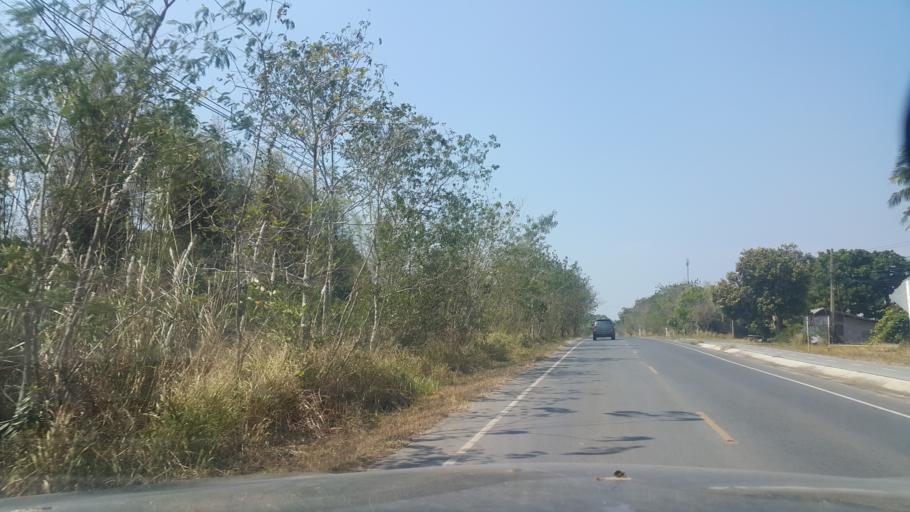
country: TH
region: Nakhon Ratchasima
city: Wang Nam Khiao
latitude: 14.3654
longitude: 101.9089
